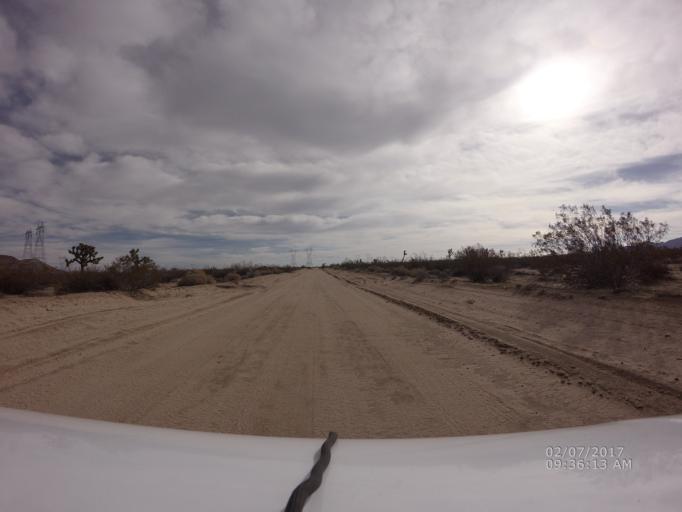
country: US
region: California
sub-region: San Bernardino County
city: Pinon Hills
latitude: 34.5275
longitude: -117.7155
